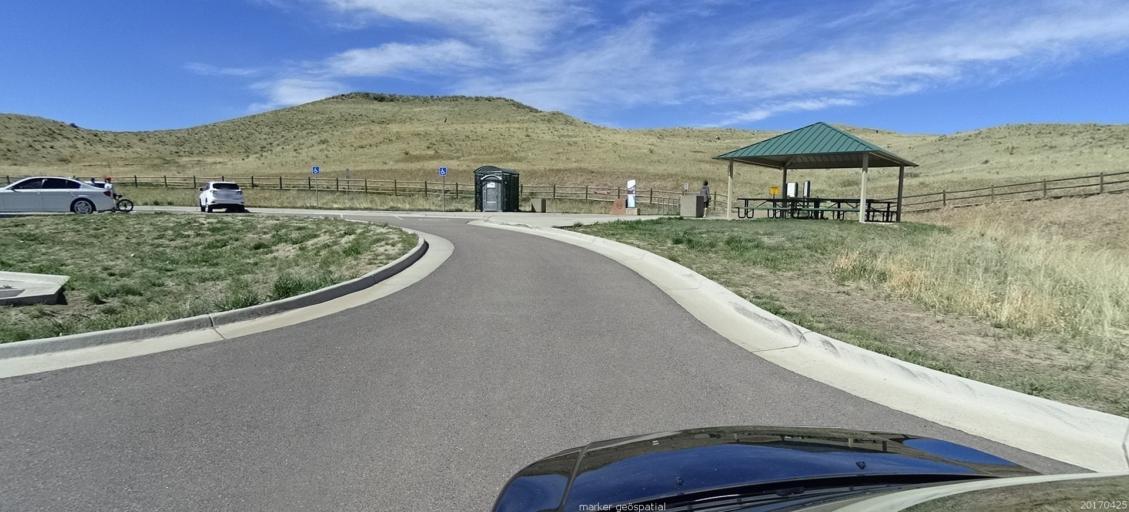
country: US
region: Colorado
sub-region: Douglas County
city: Carriage Club
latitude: 39.5285
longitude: -104.8864
